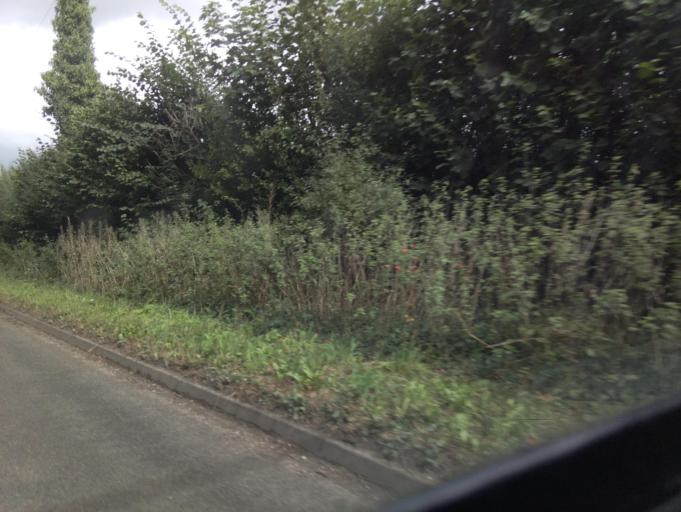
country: GB
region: England
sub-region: Staffordshire
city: Eccleshall
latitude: 52.8745
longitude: -2.2448
